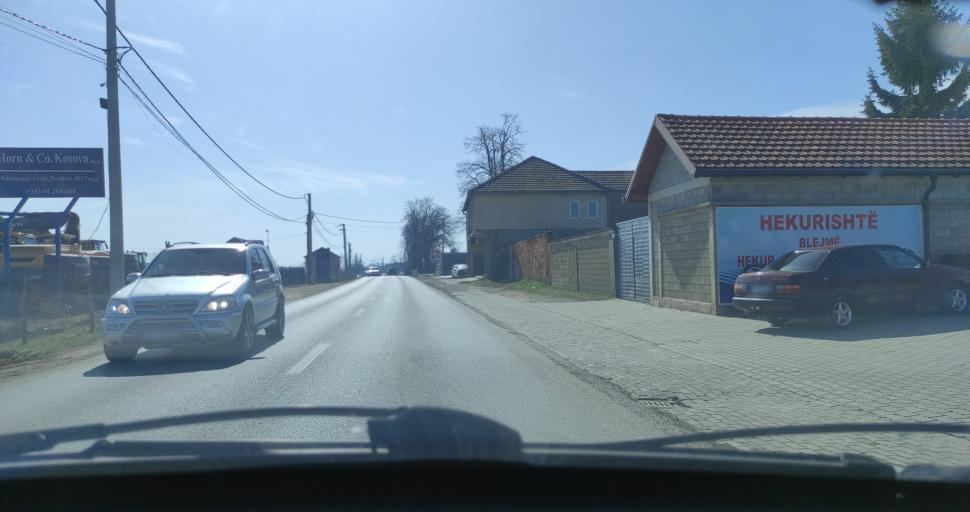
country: XK
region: Gjakova
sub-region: Komuna e Decanit
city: Lebushe
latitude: 42.5695
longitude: 20.2929
